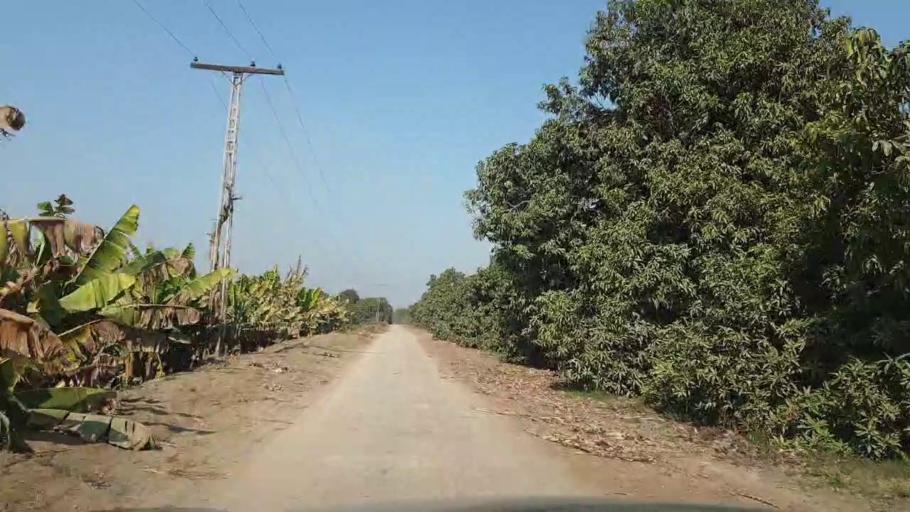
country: PK
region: Sindh
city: Tando Allahyar
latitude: 25.5566
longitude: 68.7092
